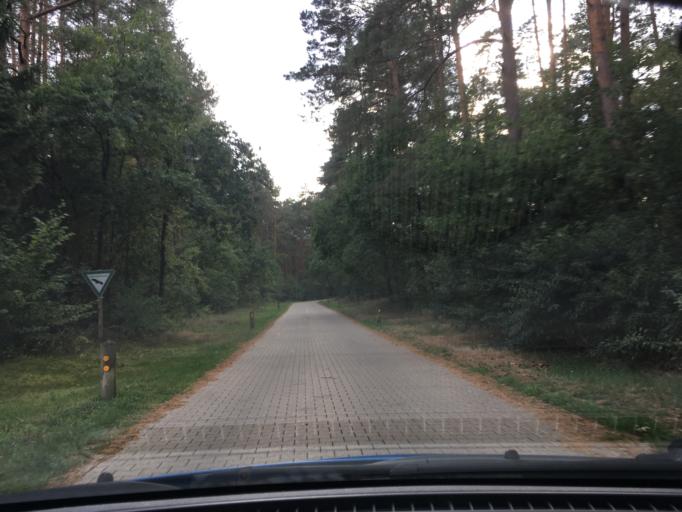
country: DE
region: Lower Saxony
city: Garstedt
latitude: 53.2849
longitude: 10.1502
